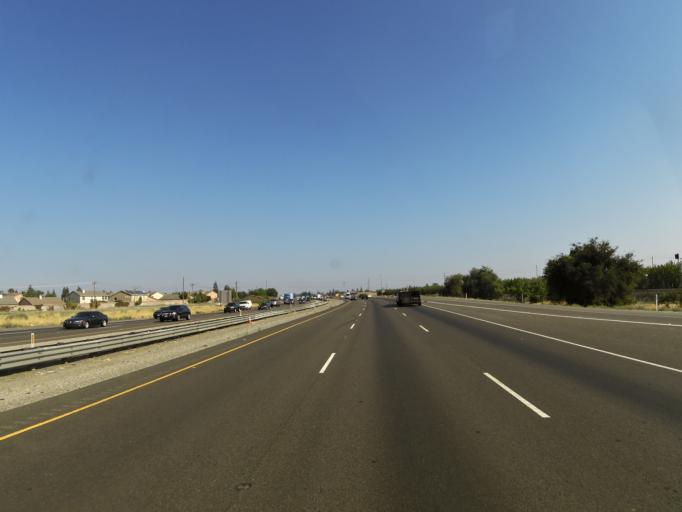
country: US
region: California
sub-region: Stanislaus County
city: Salida
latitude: 37.7238
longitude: -121.1016
